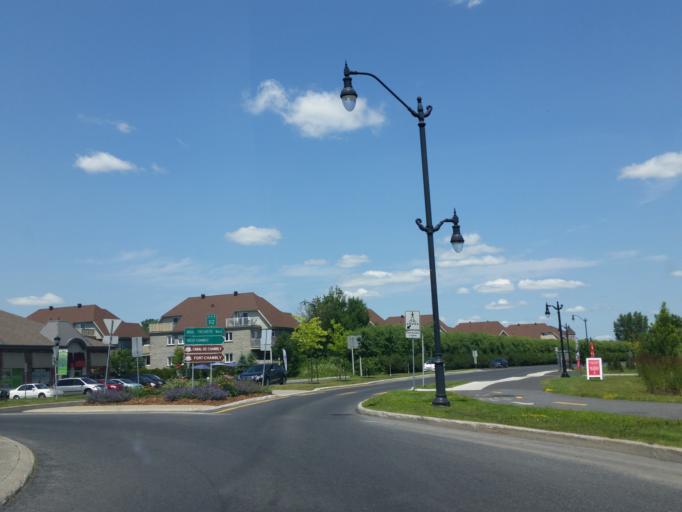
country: CA
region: Quebec
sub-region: Monteregie
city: Carignan
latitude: 45.4275
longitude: -73.3100
